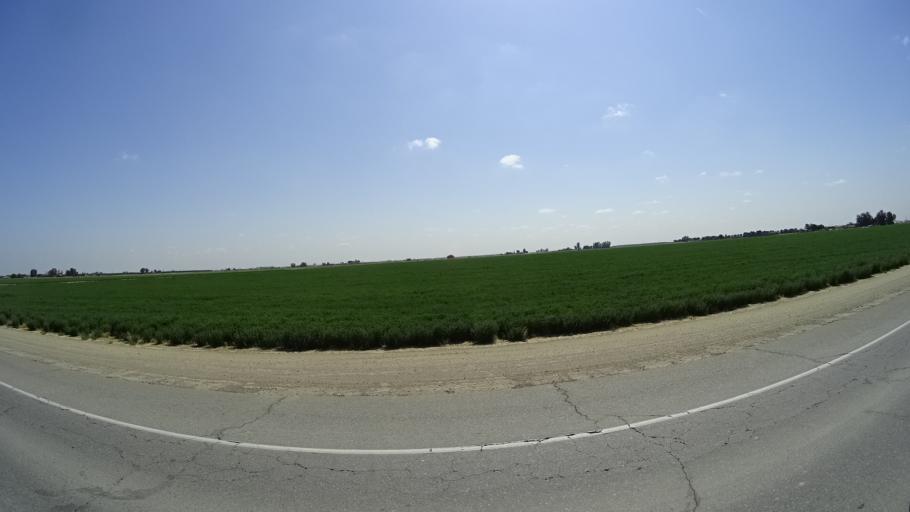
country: US
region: California
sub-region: Kings County
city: Home Garden
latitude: 36.2758
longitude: -119.6370
